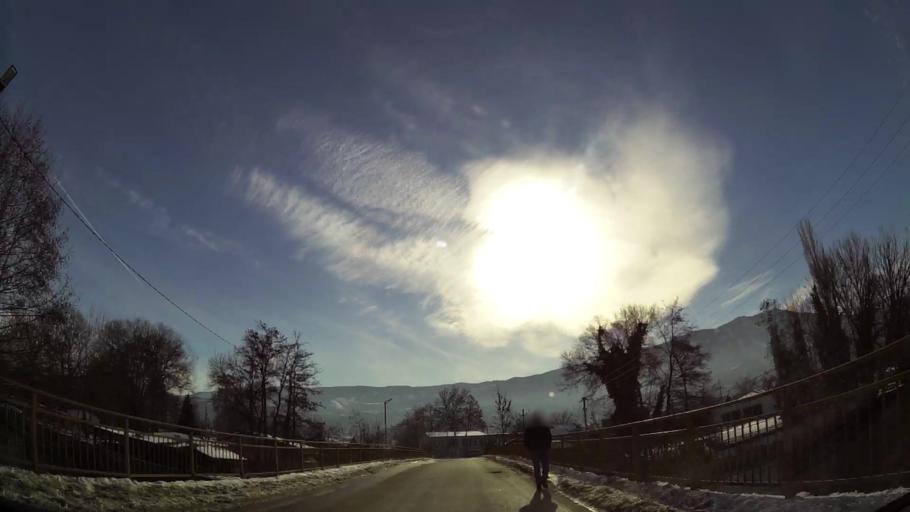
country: MK
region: Saraj
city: Saraj
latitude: 41.9956
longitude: 21.3270
